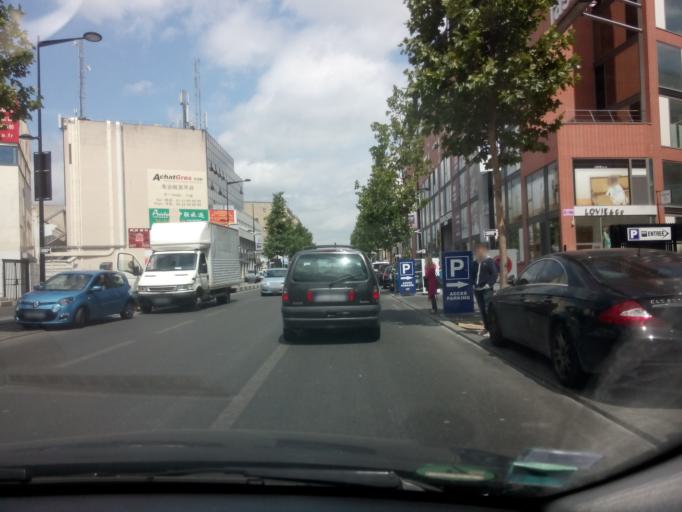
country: FR
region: Ile-de-France
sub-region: Departement de Seine-Saint-Denis
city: Aubervilliers
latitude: 48.9051
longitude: 2.3740
